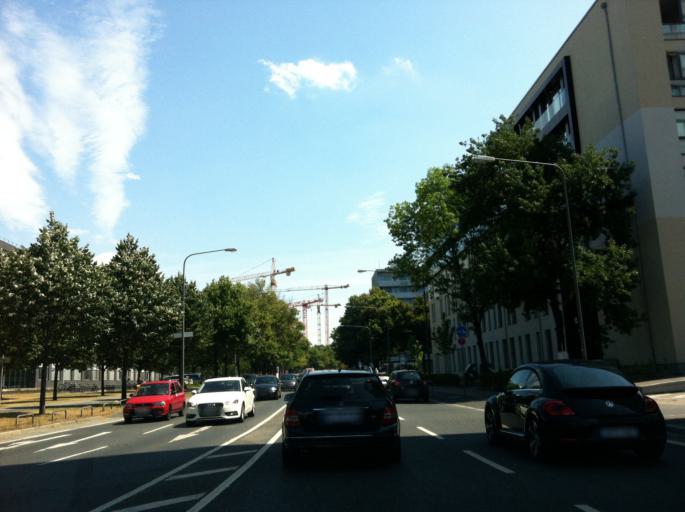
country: DE
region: Hesse
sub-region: Regierungsbezirk Darmstadt
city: Frankfurt am Main
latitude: 50.1317
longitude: 8.6729
